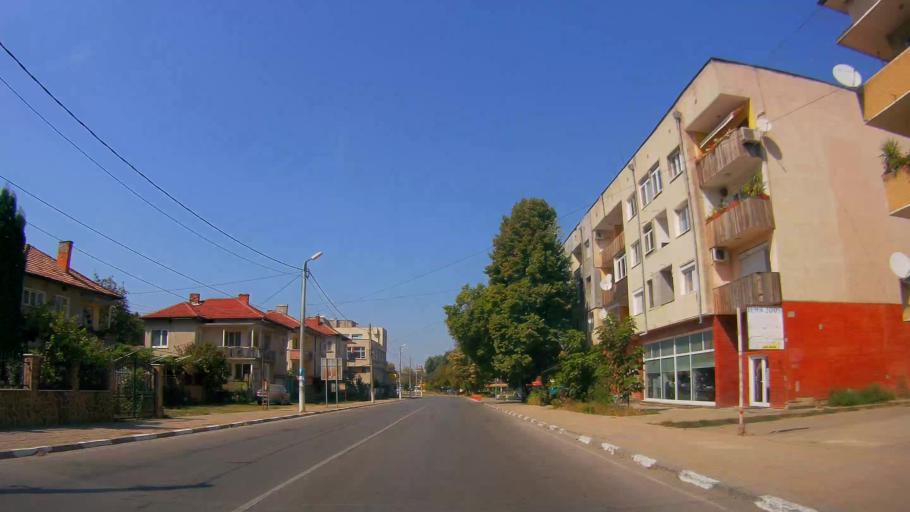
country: BG
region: Razgrad
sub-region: Obshtina Tsar Kaloyan
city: Tsar Kaloyan
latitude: 43.6076
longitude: 26.2384
